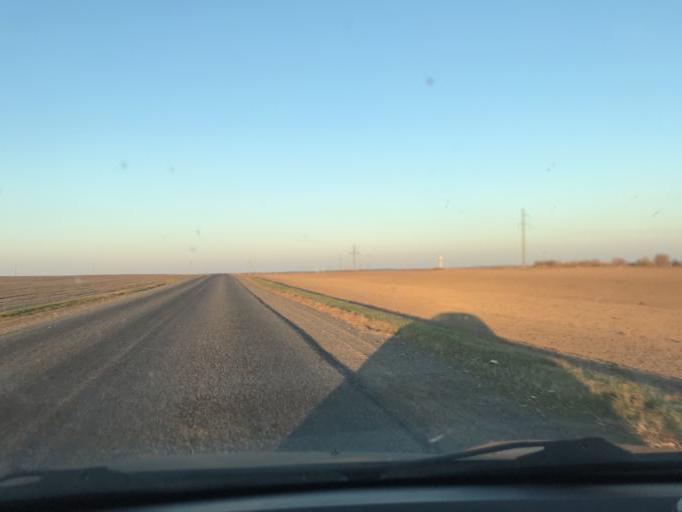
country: BY
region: Gomel
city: Brahin
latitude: 51.8351
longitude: 30.3271
